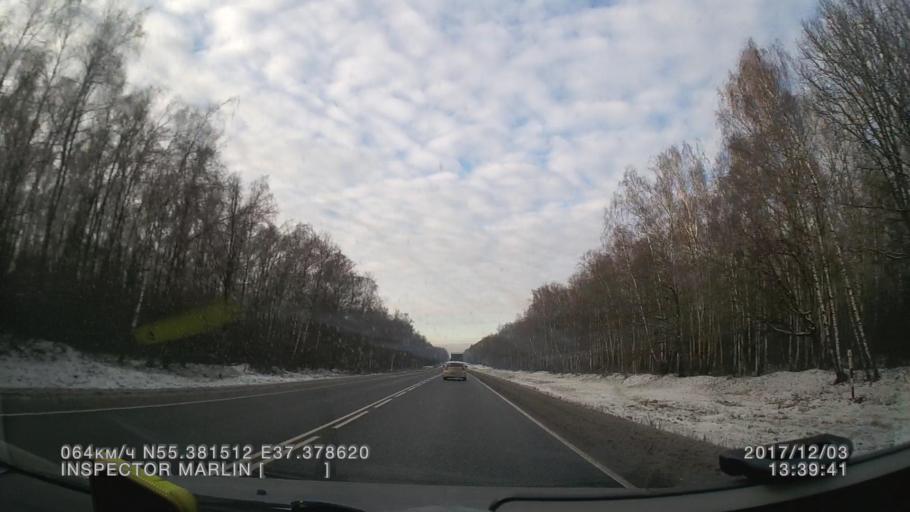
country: RU
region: Moskovskaya
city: Dubrovitsy
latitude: 55.3816
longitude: 37.3784
